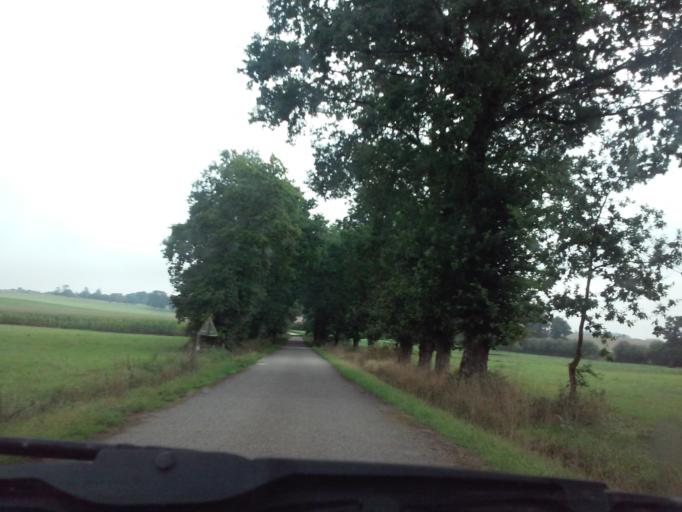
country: FR
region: Brittany
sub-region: Departement du Morbihan
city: Guilliers
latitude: 48.0120
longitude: -2.4430
